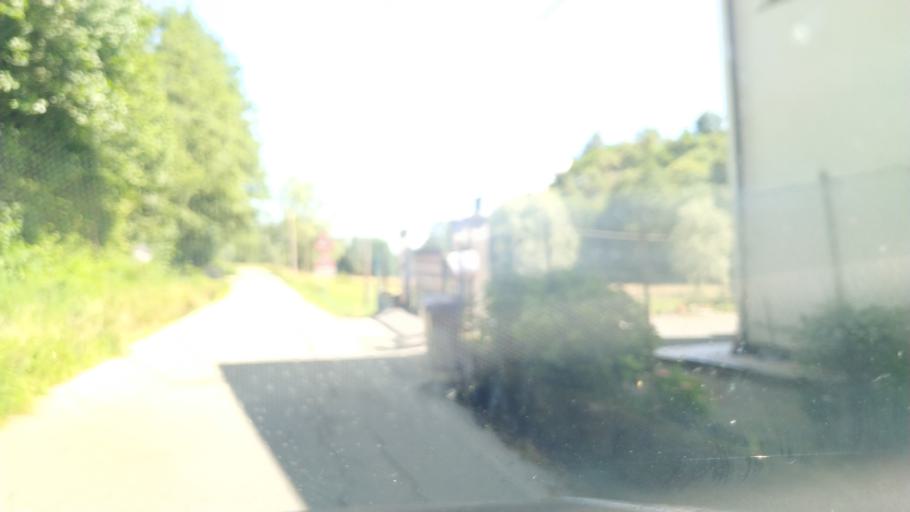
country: IT
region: Piedmont
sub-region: Provincia di Torino
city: Baldissero Canavese
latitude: 45.4089
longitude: 7.7207
